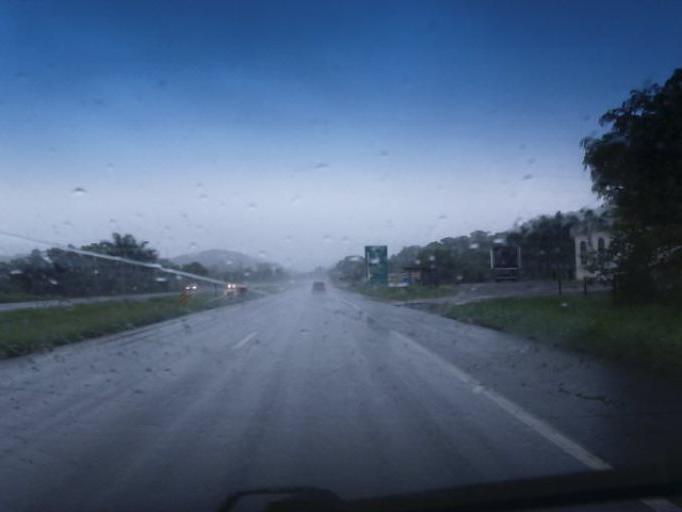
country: BR
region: Sao Paulo
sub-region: Juquia
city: Juquia
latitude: -24.3562
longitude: -47.6816
